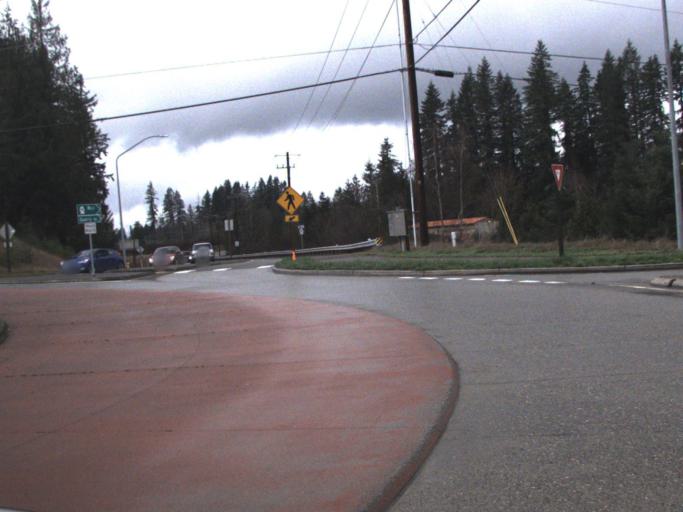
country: US
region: Washington
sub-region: Snohomish County
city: Granite Falls
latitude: 48.0915
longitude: -121.9799
